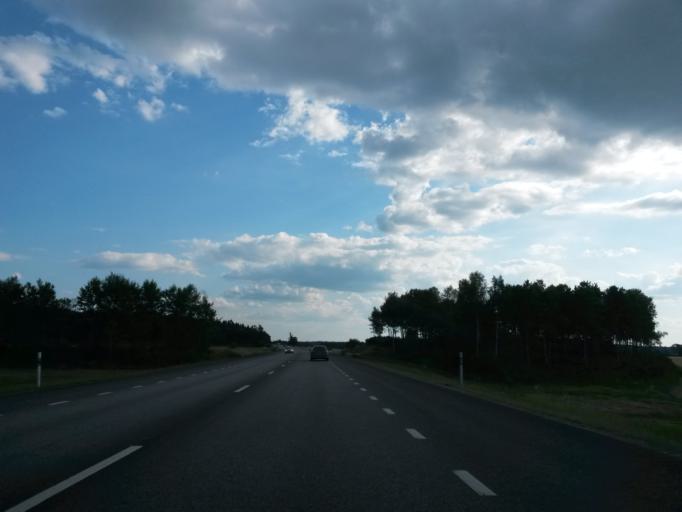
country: SE
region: Vaestra Goetaland
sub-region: Vargarda Kommun
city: Vargarda
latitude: 58.1179
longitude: 12.8464
